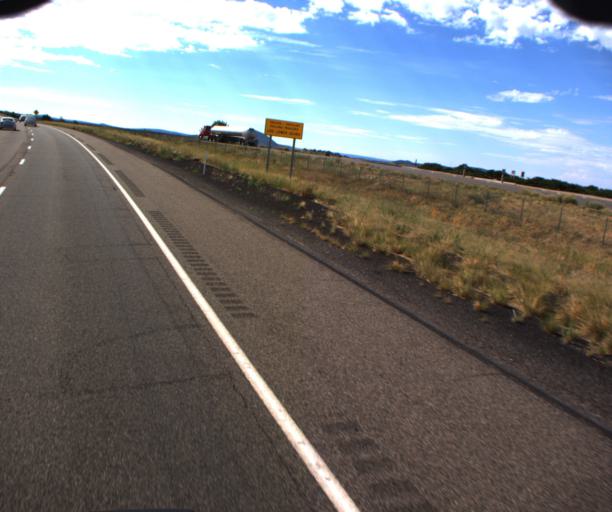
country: US
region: Arizona
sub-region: Yavapai County
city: Village of Oak Creek (Big Park)
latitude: 34.8129
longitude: -111.6105
